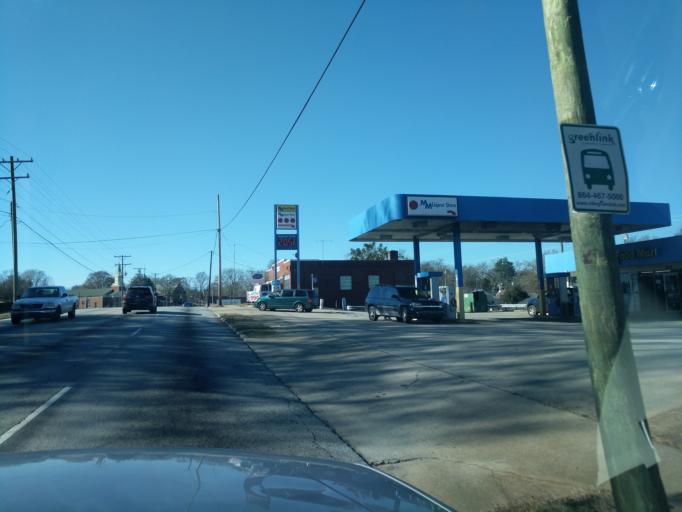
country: US
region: South Carolina
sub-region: Greenville County
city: Judson
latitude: 34.8397
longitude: -82.4273
